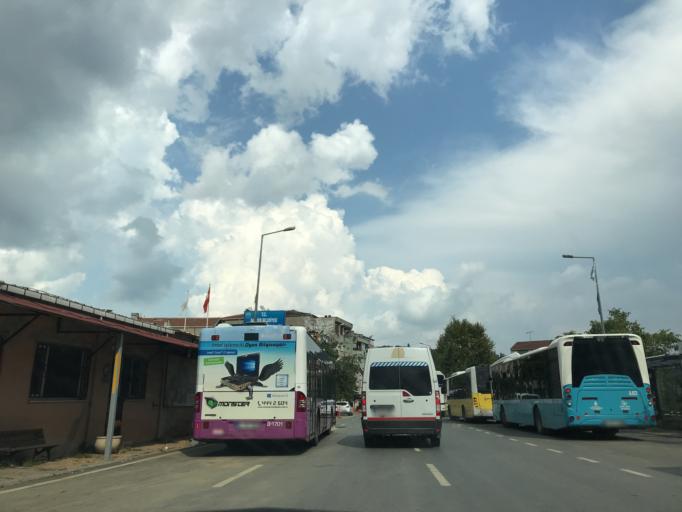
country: TR
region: Istanbul
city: Arikoey
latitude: 41.1730
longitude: 29.0477
